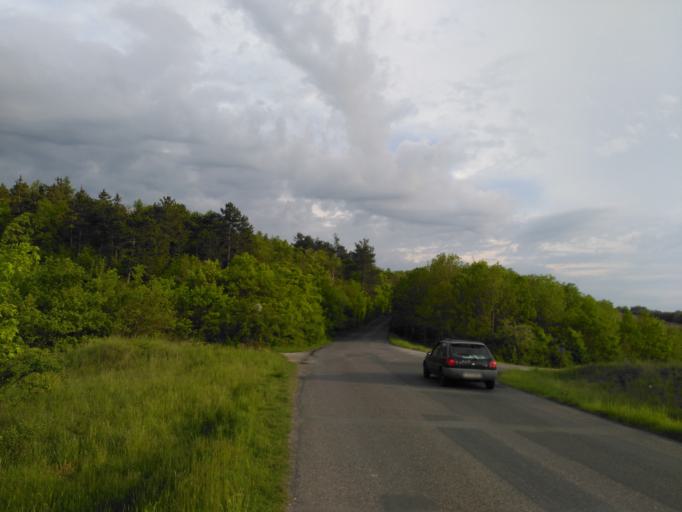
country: CZ
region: Central Bohemia
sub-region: Okres Beroun
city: Beroun
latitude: 49.9142
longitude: 14.0754
